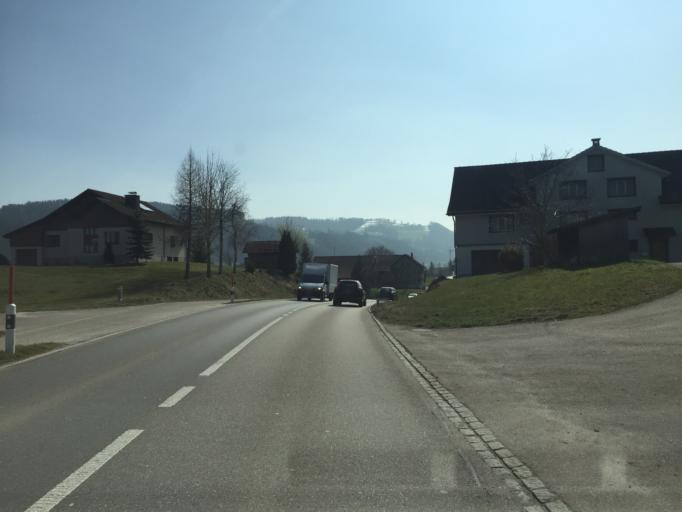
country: CH
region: Saint Gallen
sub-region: Wahlkreis Toggenburg
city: Lutisburg
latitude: 47.3815
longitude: 9.0729
